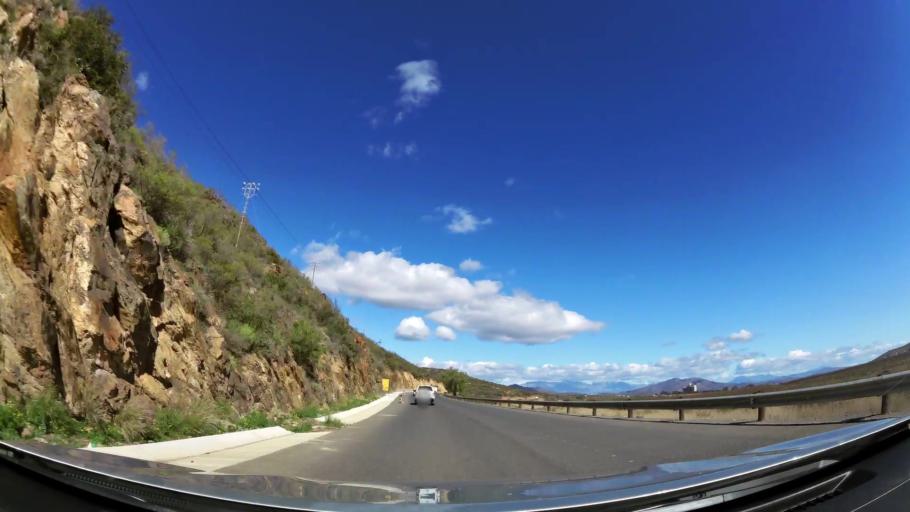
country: ZA
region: Western Cape
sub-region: Cape Winelands District Municipality
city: Ashton
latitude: -33.8237
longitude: 20.0906
